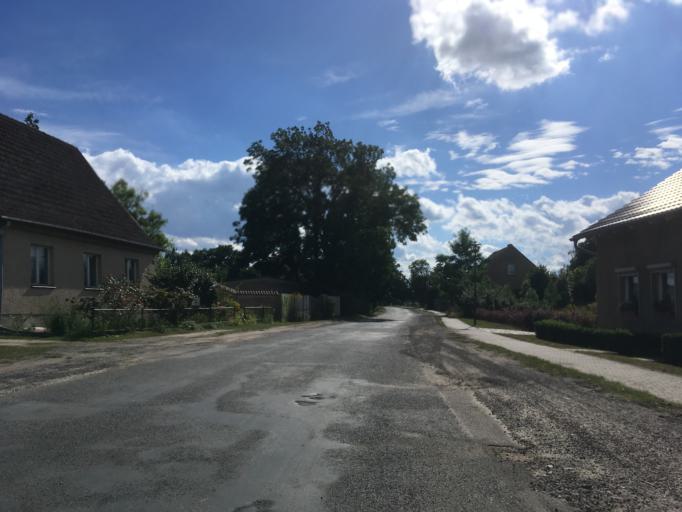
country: DE
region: Brandenburg
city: Angermunde
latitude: 52.9747
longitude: 13.9871
